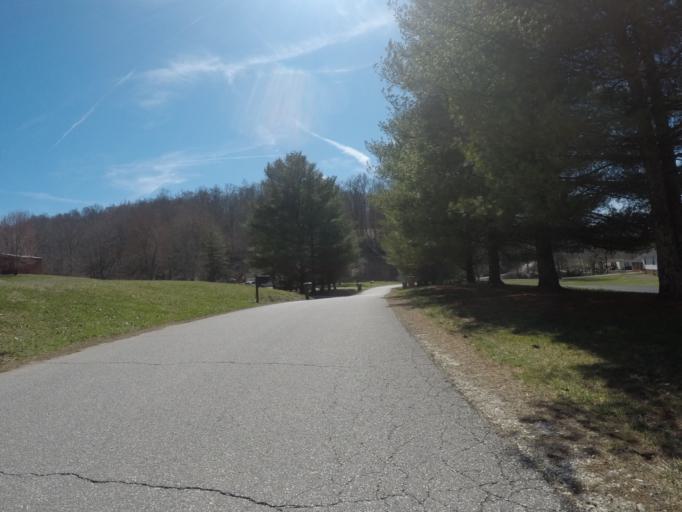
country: US
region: Ohio
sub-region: Lawrence County
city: South Point
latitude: 38.4738
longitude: -82.5652
